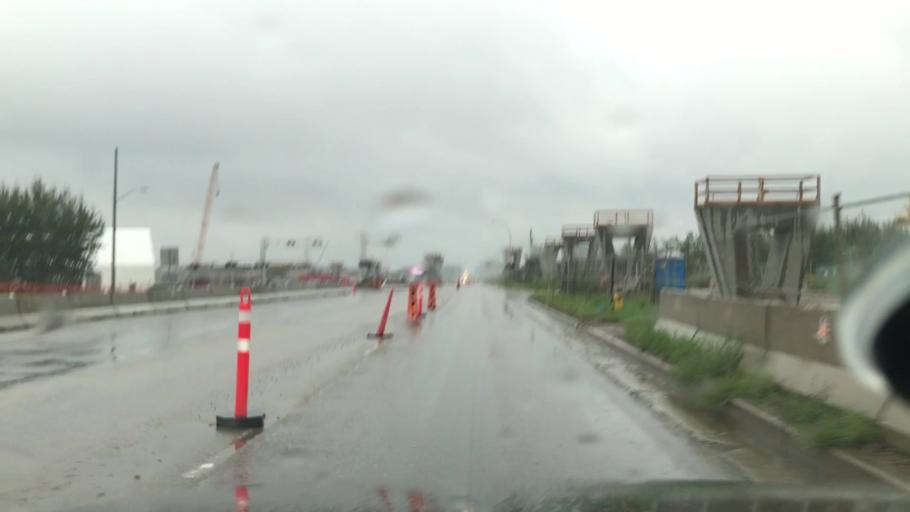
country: CA
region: Alberta
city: Edmonton
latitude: 53.4967
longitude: -113.4426
